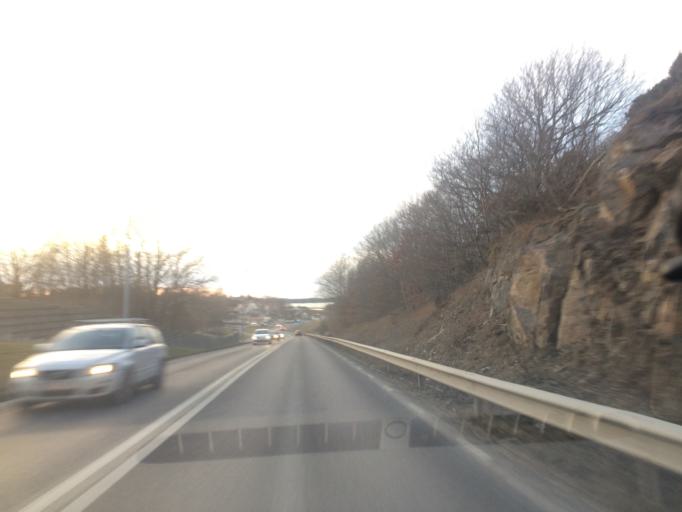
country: SE
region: Vaestra Goetaland
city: Hjuvik
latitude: 57.7112
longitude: 11.7297
